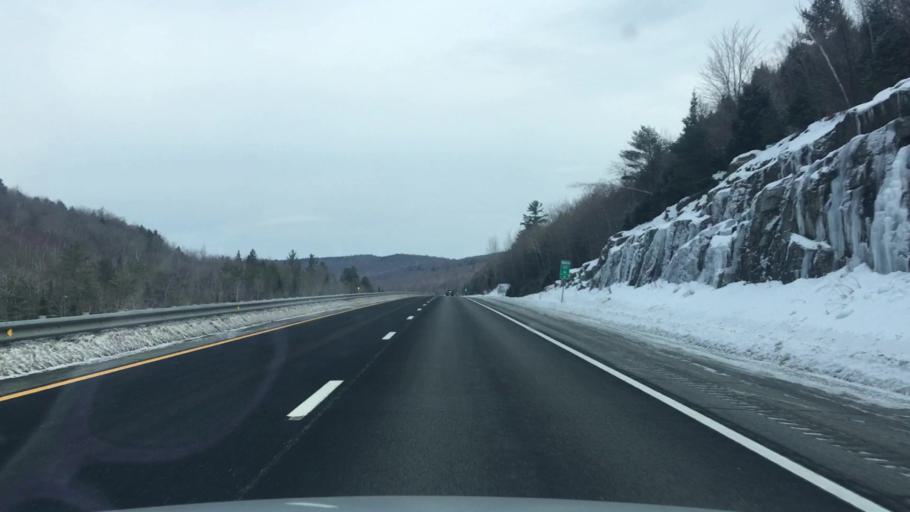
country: US
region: New Hampshire
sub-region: Sullivan County
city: Grantham
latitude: 43.5488
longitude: -72.1398
